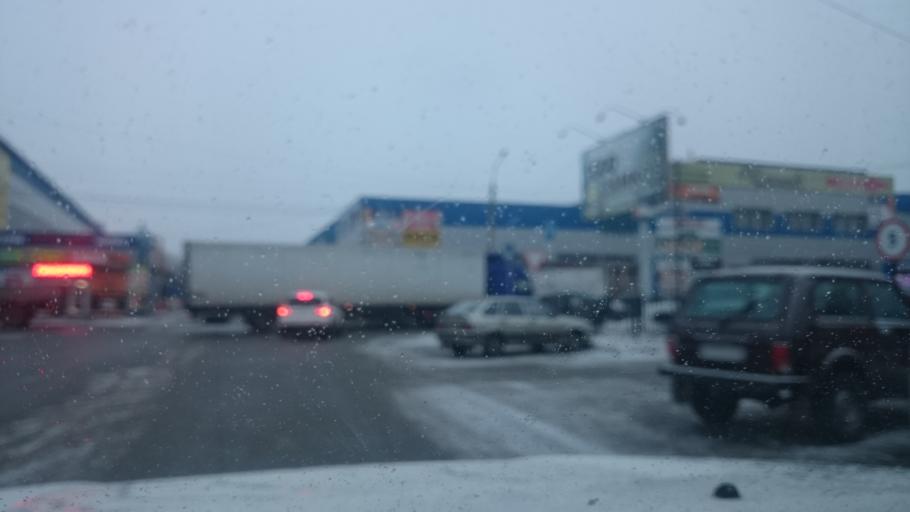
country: RU
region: Tula
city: Tula
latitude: 54.2026
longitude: 37.5922
